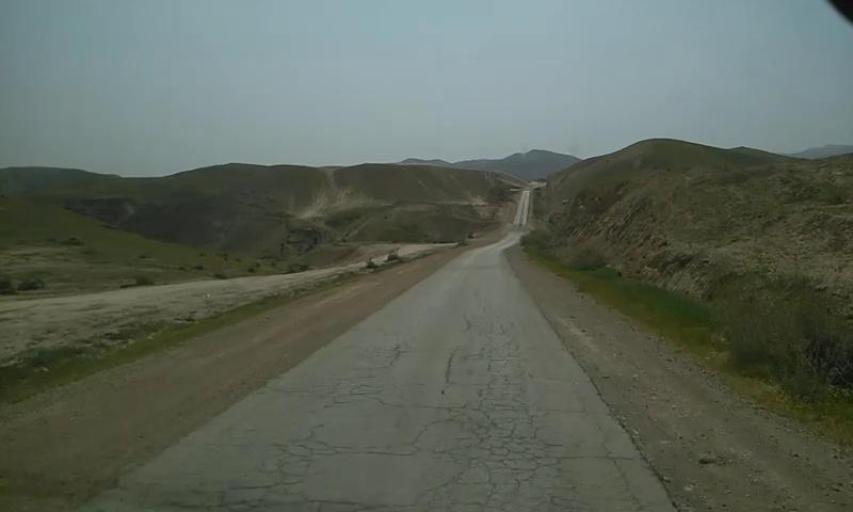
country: PS
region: West Bank
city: Jericho
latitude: 31.7852
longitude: 35.4292
